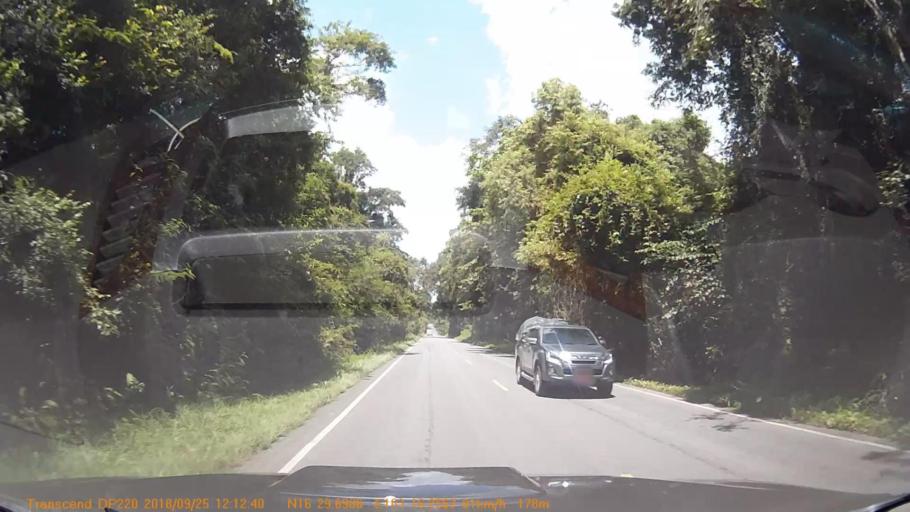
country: TH
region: Kalasin
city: Huai Mek
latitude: 16.4950
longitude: 103.2709
